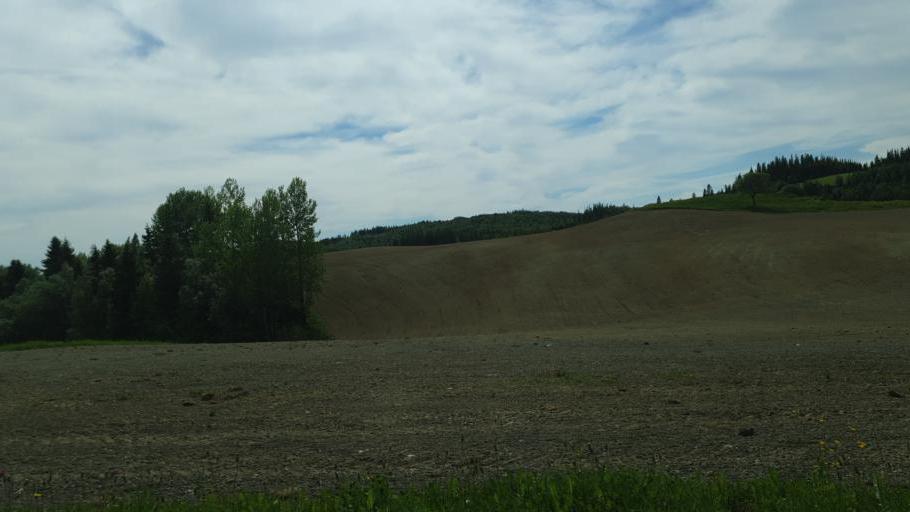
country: NO
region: Nord-Trondelag
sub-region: Leksvik
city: Leksvik
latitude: 63.6854
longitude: 10.5697
